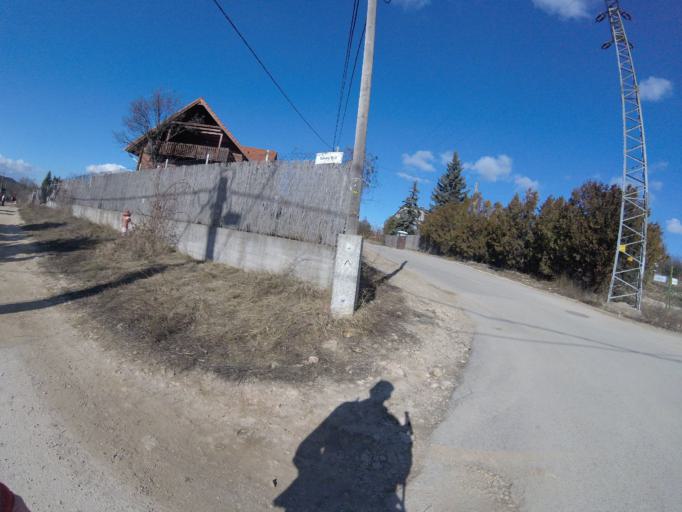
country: HU
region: Pest
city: Pilisszentivan
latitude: 47.5839
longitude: 18.8996
